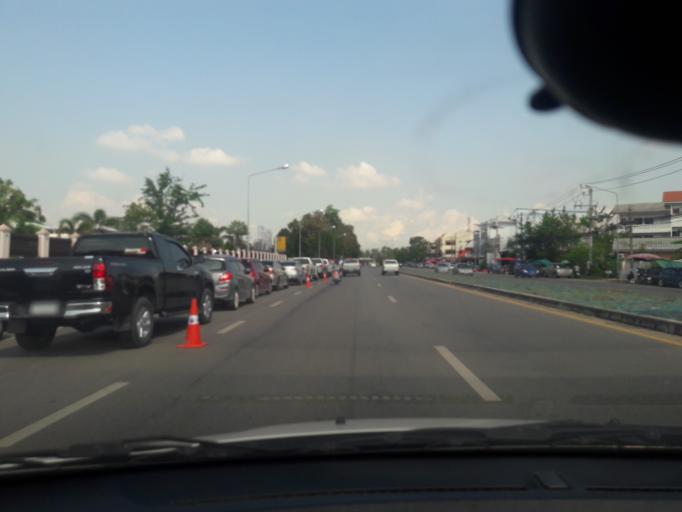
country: TH
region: Lampang
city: Lampang
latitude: 18.2309
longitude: 99.4904
